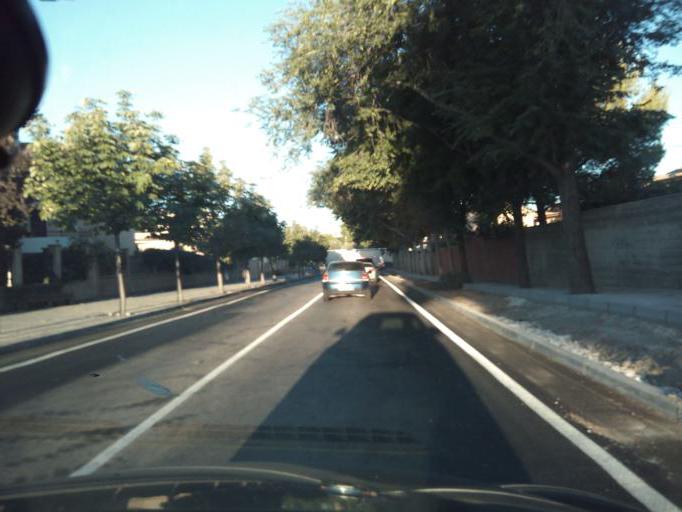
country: ES
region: Madrid
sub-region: Provincia de Madrid
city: Daganzo de Arriba
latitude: 40.5423
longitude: -3.4613
